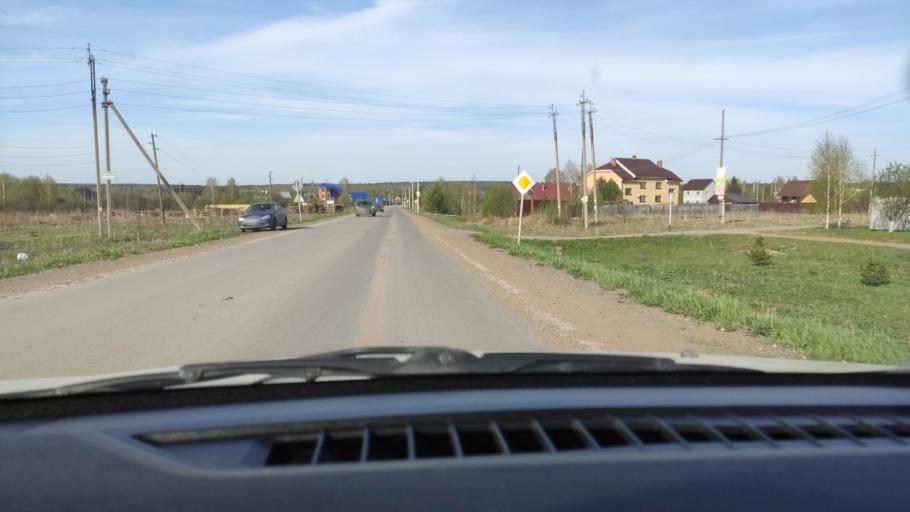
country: RU
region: Perm
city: Sylva
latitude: 57.9296
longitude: 56.6893
